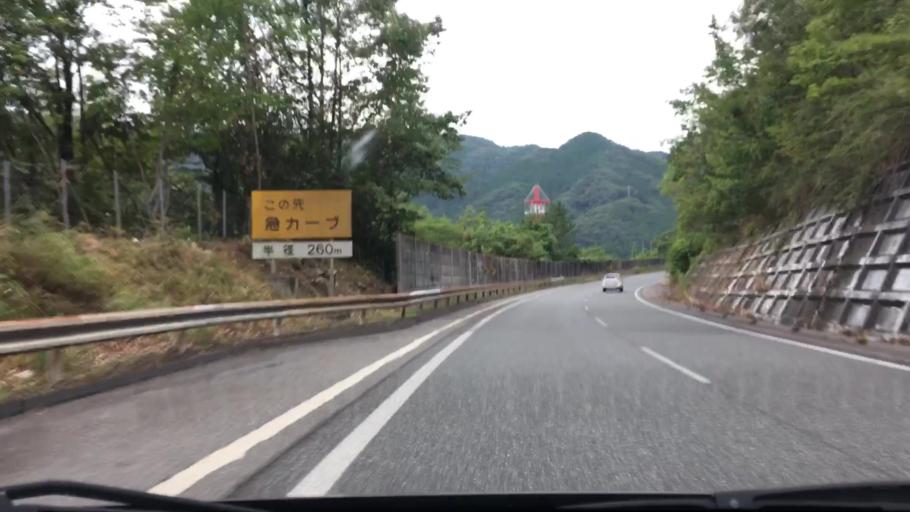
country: JP
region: Okayama
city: Niimi
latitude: 34.9908
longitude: 133.4653
